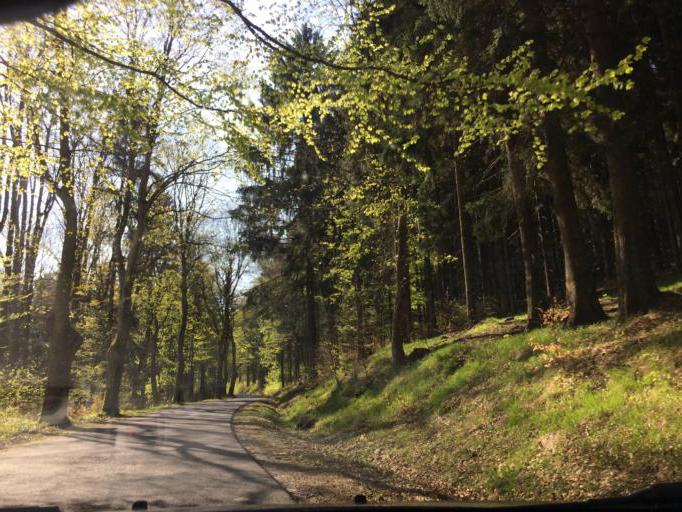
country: PL
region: Lower Silesian Voivodeship
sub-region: Powiat klodzki
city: Jugow
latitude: 50.6693
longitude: 16.5168
